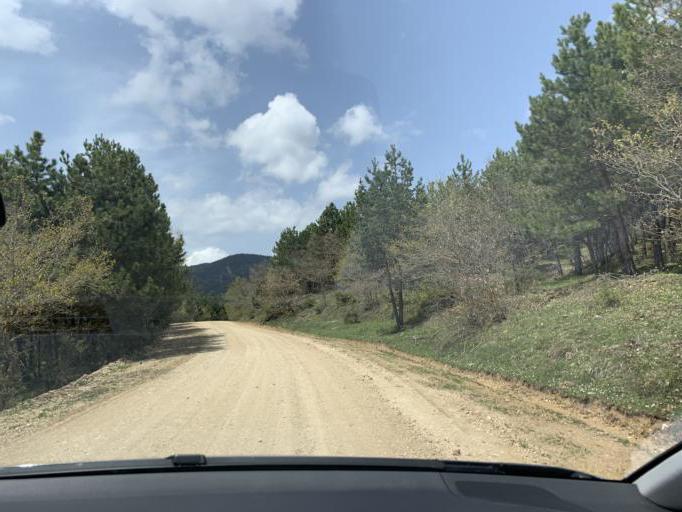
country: TR
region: Bolu
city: Bolu
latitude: 40.8302
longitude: 31.6759
